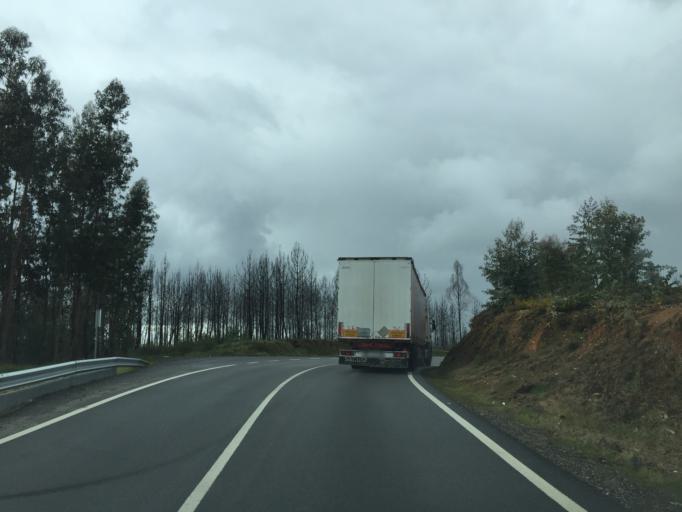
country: PT
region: Coimbra
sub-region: Oliveira do Hospital
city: Oliveira do Hospital
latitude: 40.3251
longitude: -7.9301
